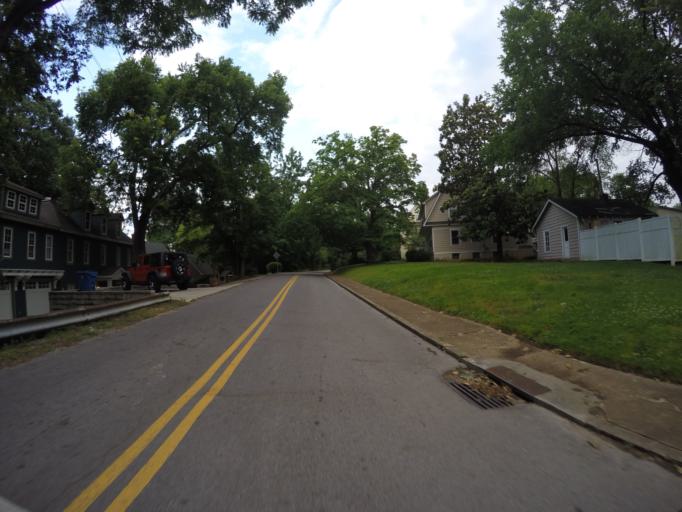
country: US
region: Tennessee
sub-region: Davidson County
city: Lakewood
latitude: 36.2597
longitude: -86.6434
